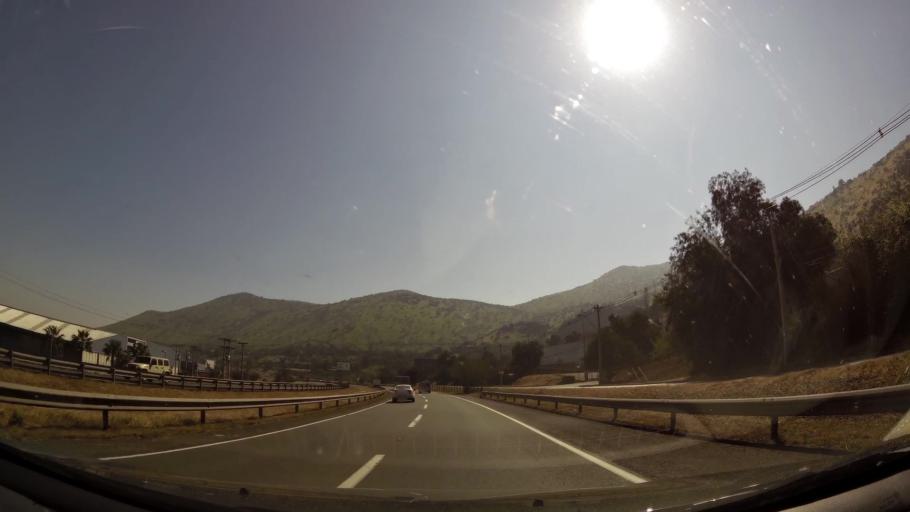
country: CL
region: Santiago Metropolitan
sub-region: Provincia de Chacabuco
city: Chicureo Abajo
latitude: -33.3397
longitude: -70.6926
